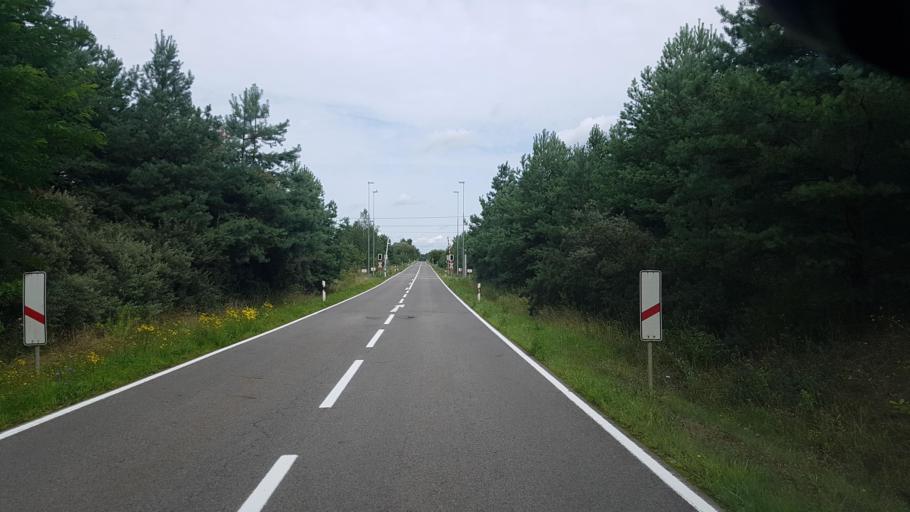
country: DE
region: Brandenburg
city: Spremberg
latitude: 51.6077
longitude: 14.3419
